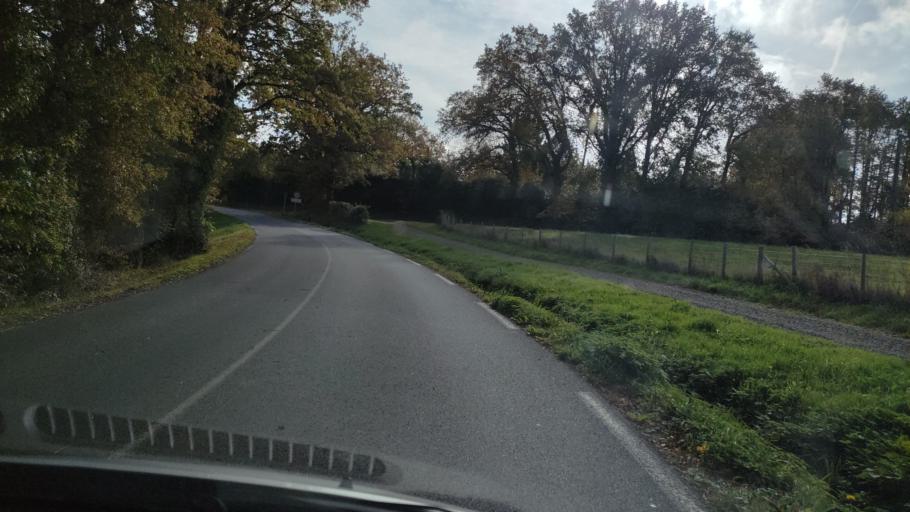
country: FR
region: Limousin
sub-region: Departement de la Haute-Vienne
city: Isle
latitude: 45.8134
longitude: 1.2144
